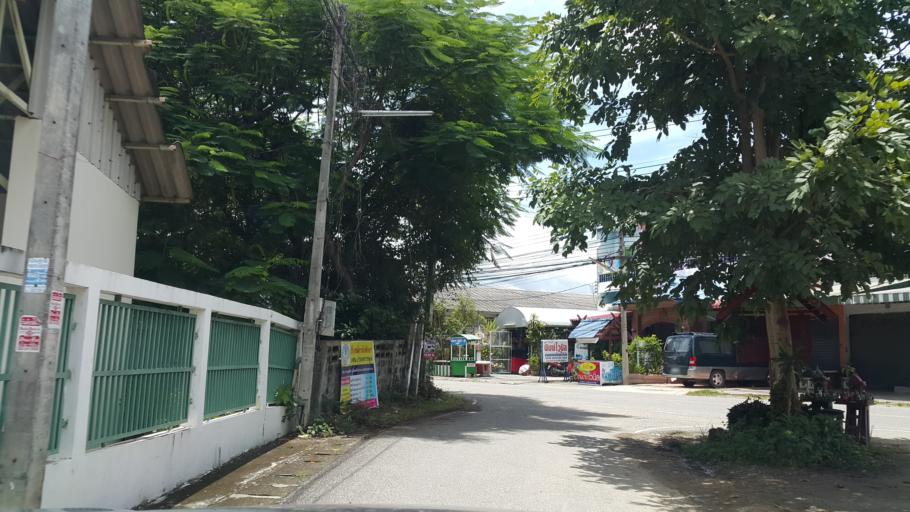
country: TH
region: Chiang Mai
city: San Kamphaeng
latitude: 18.7404
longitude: 99.1290
